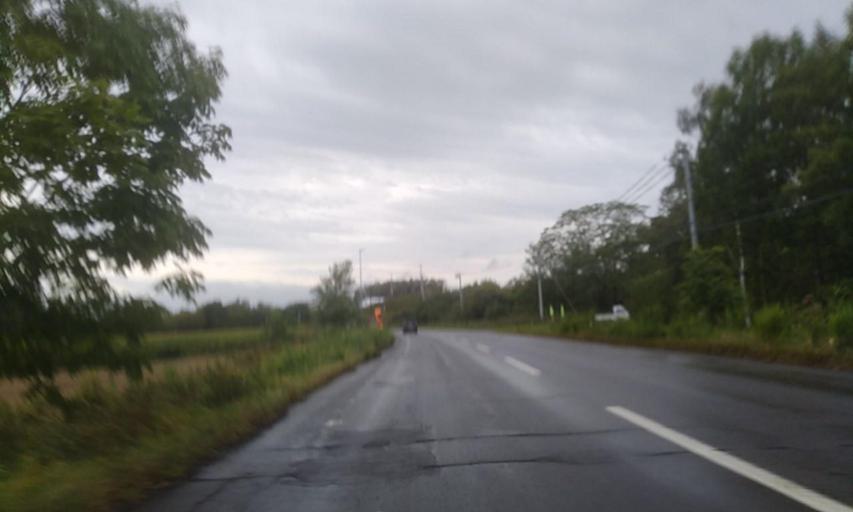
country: JP
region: Hokkaido
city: Abashiri
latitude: 44.0482
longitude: 144.1017
